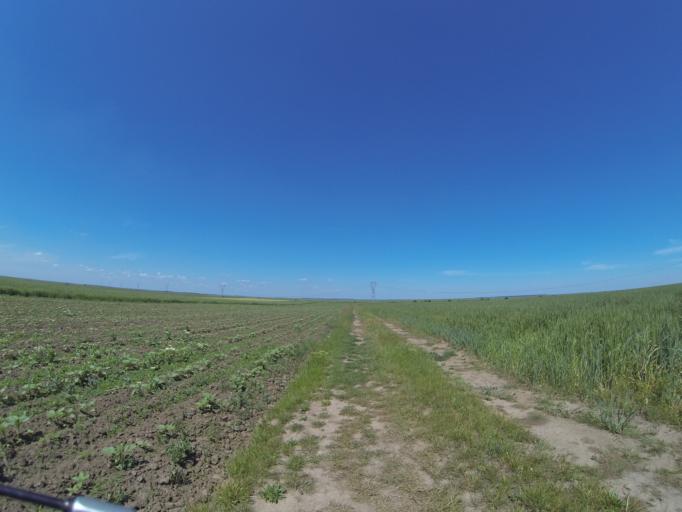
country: RO
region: Dolj
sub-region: Comuna Leu
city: Leu
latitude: 44.2074
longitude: 24.0353
